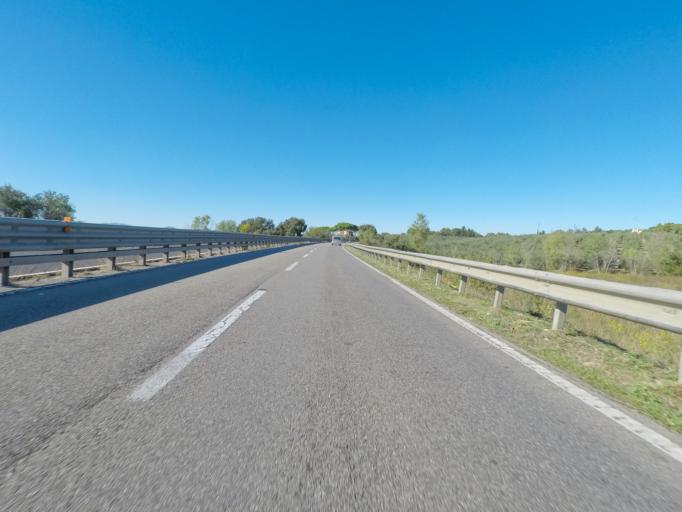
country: IT
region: Tuscany
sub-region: Provincia di Grosseto
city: Grosseto
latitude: 42.7212
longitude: 11.1391
